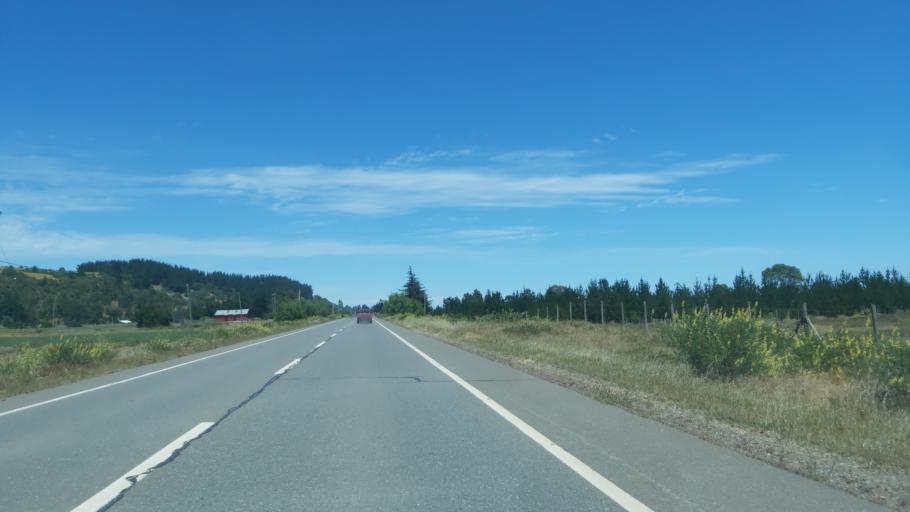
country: CL
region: Maule
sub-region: Provincia de Talca
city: Constitucion
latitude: -35.1651
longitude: -72.2603
